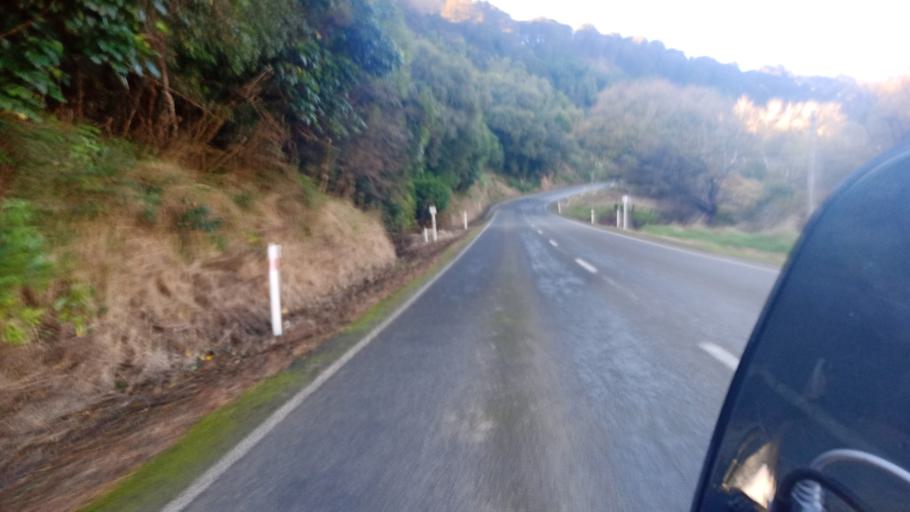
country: NZ
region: Hawke's Bay
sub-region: Wairoa District
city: Wairoa
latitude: -38.8638
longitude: 177.1968
